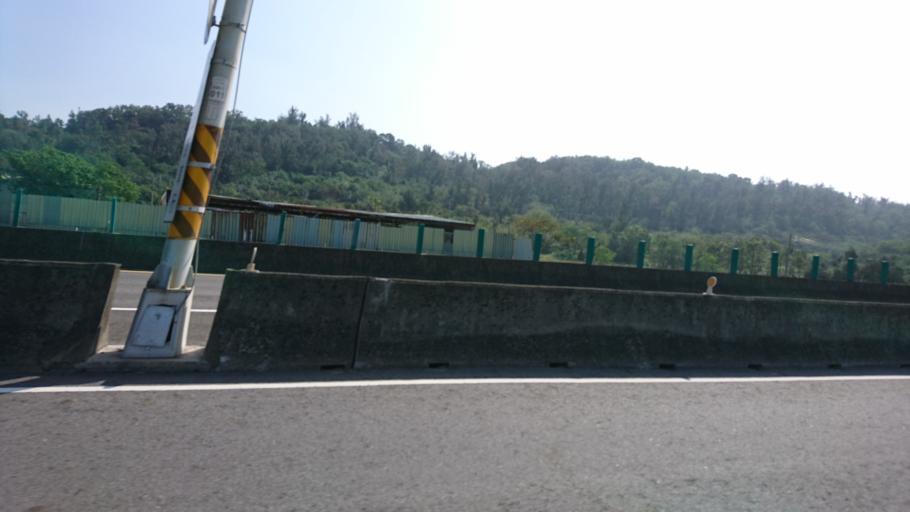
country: TW
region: Taiwan
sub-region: Hsinchu
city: Hsinchu
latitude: 24.7362
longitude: 120.8847
